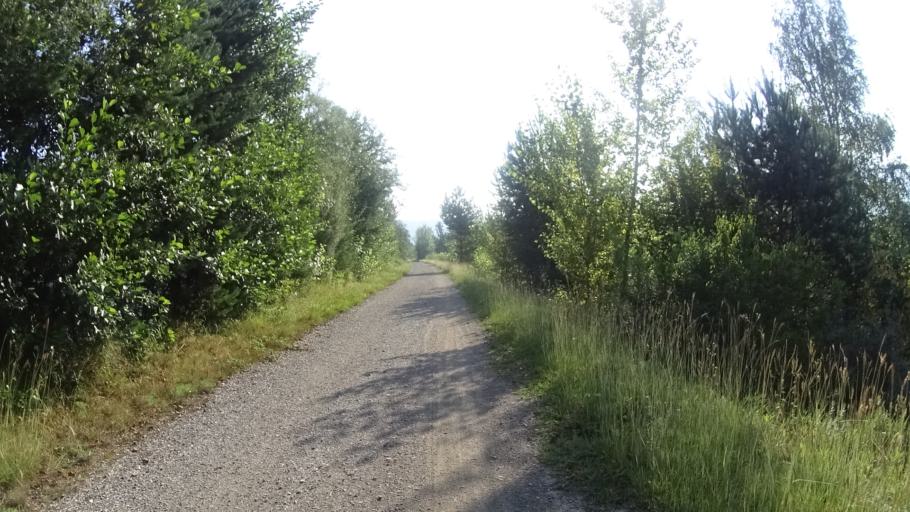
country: AT
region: Carinthia
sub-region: Politischer Bezirk Klagenfurt Land
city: Maria Rain
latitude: 46.5426
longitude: 14.2664
